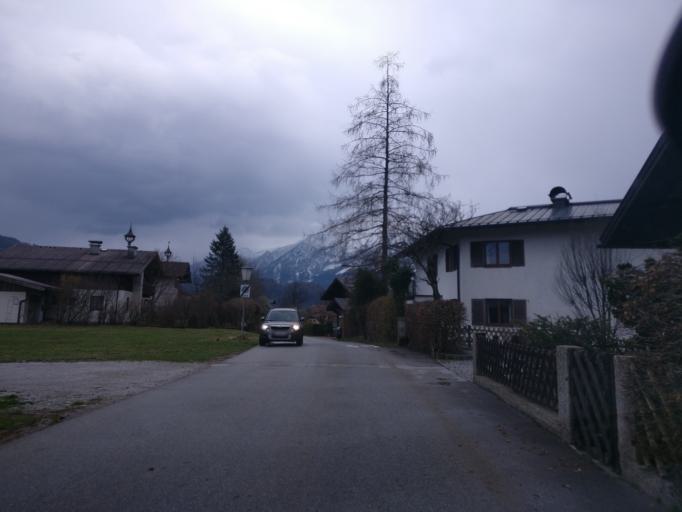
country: AT
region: Salzburg
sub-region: Politischer Bezirk Hallein
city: Kuchl
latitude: 47.6202
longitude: 13.1494
